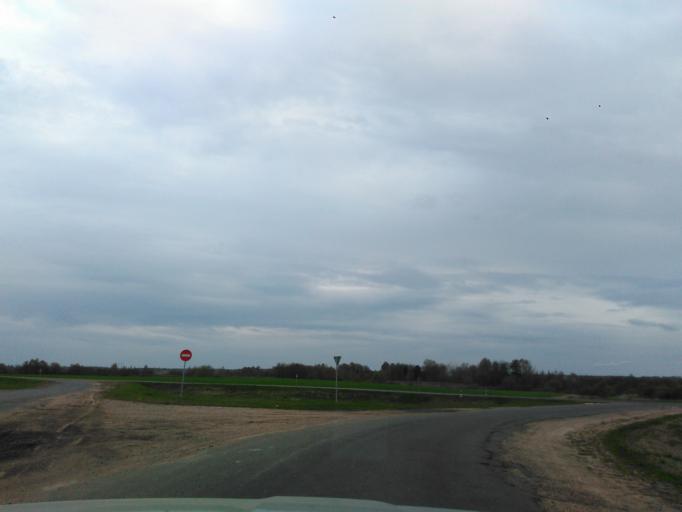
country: BY
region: Vitebsk
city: Chashniki
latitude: 54.7896
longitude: 29.1334
